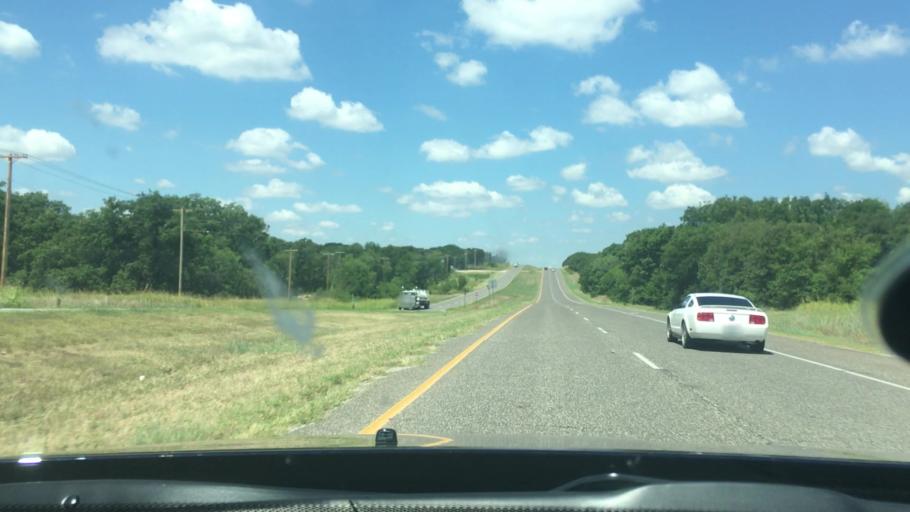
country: US
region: Oklahoma
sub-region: Carter County
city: Lone Grove
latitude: 34.1731
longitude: -97.2854
